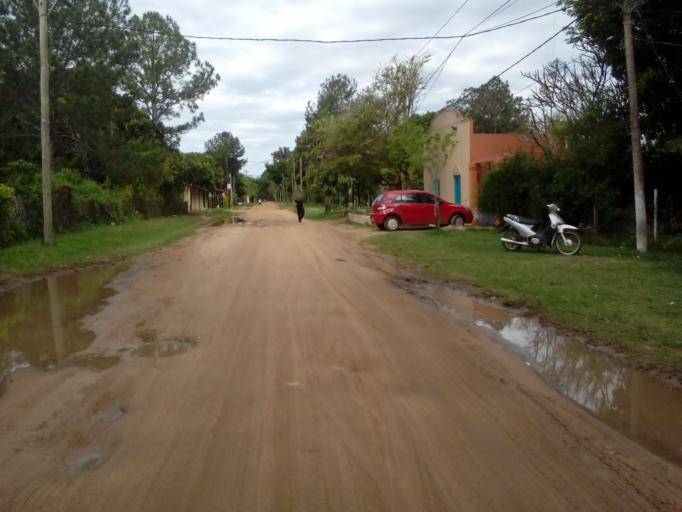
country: AR
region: Corrientes
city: San Luis del Palmar
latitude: -27.4560
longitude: -58.6539
